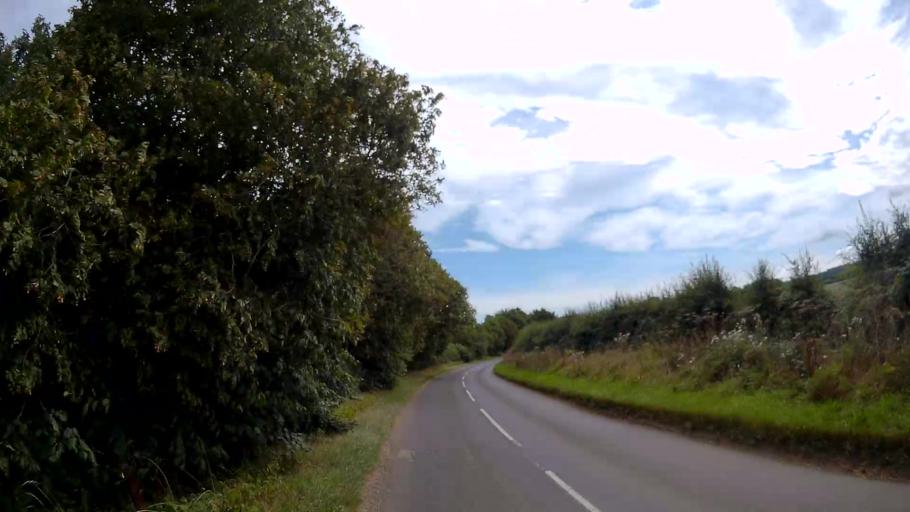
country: GB
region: England
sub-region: Hampshire
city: Long Sutton
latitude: 51.2233
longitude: -0.9475
